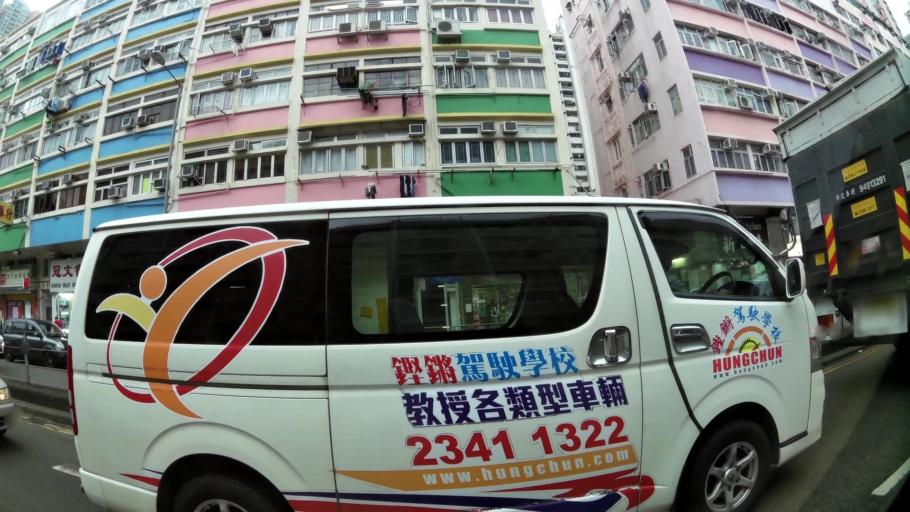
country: HK
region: Tsuen Wan
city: Tsuen Wan
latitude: 22.3722
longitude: 114.1120
